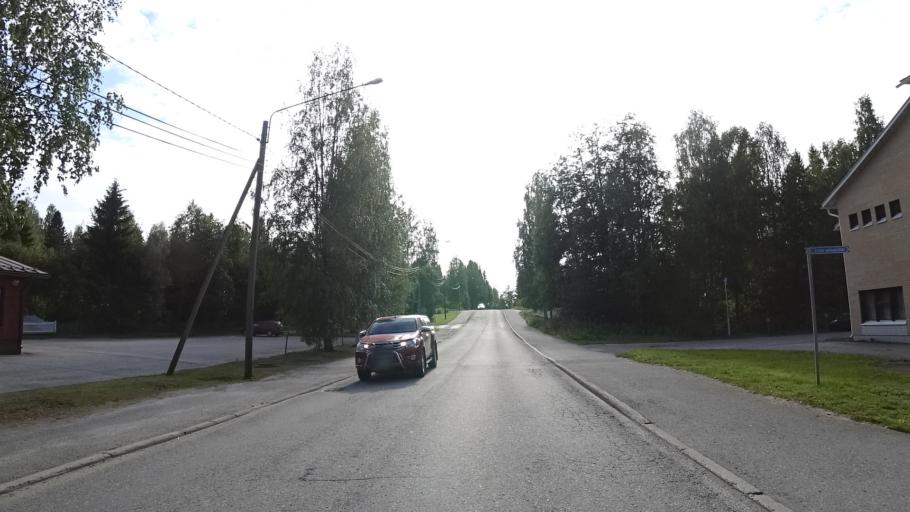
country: FI
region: North Karelia
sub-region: Joensuu
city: Eno
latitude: 62.7983
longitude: 30.1499
